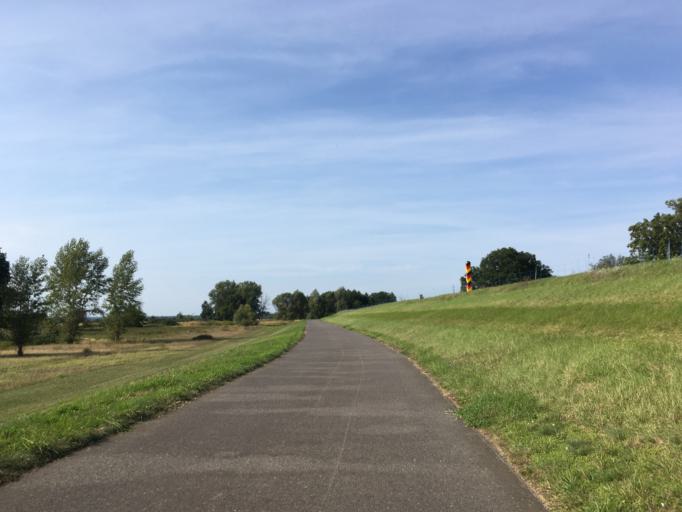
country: DE
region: Brandenburg
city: Vogelsang
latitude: 52.2273
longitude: 14.7077
